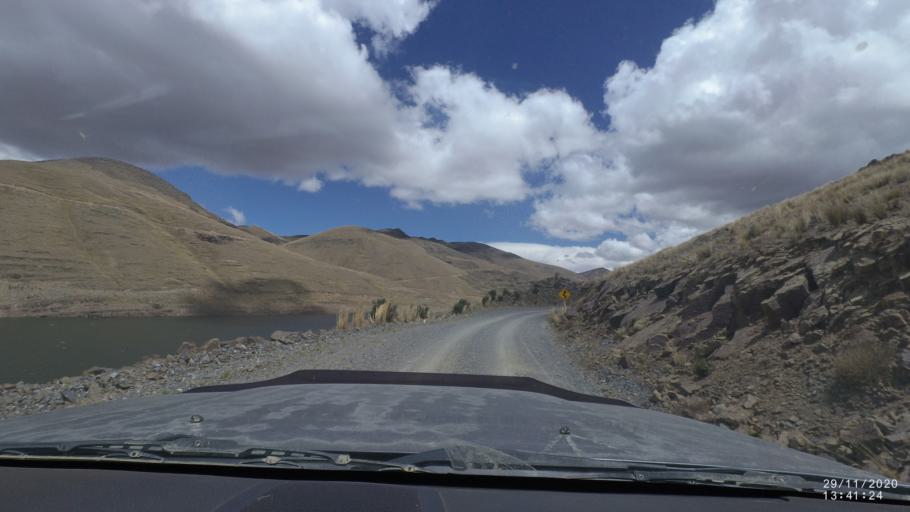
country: BO
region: Cochabamba
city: Cochabamba
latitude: -17.1316
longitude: -66.3242
